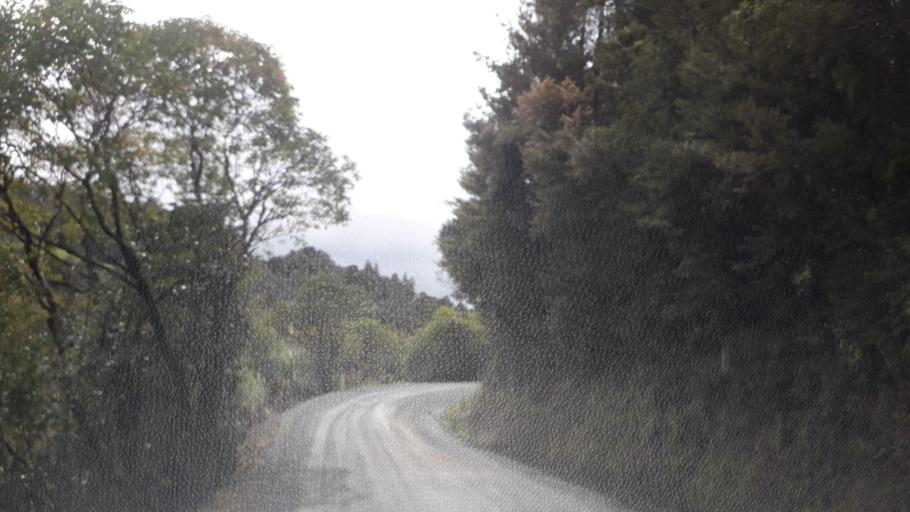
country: NZ
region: Northland
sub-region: Far North District
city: Waimate North
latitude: -35.3054
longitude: 173.5631
